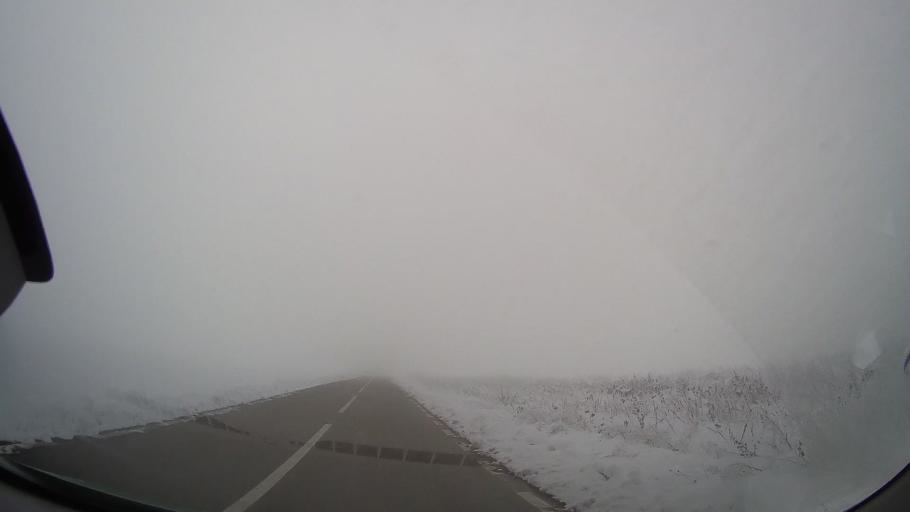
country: RO
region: Iasi
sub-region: Comuna Valea Seaca
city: Topile
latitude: 47.2736
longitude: 26.6706
